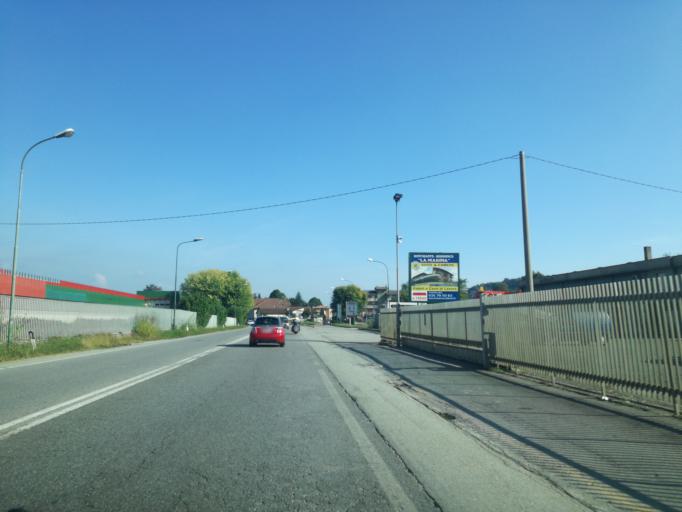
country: IT
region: Lombardy
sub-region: Provincia di Bergamo
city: Pontida
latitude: 45.7302
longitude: 9.5162
